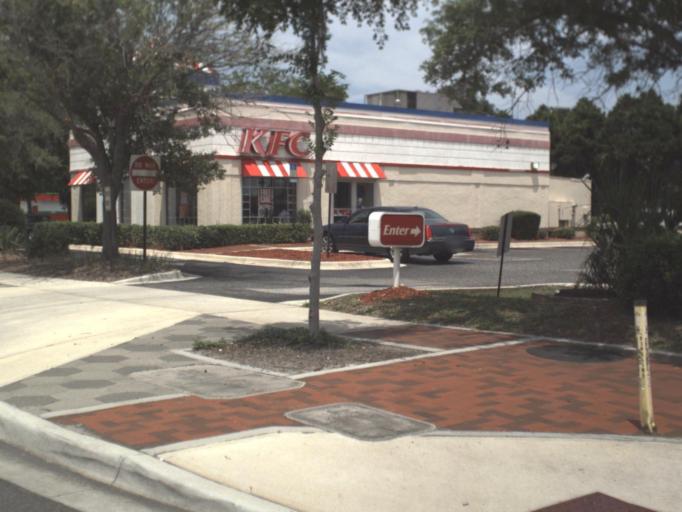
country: US
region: Florida
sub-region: Duval County
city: Jacksonville
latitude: 30.3471
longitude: -81.6537
